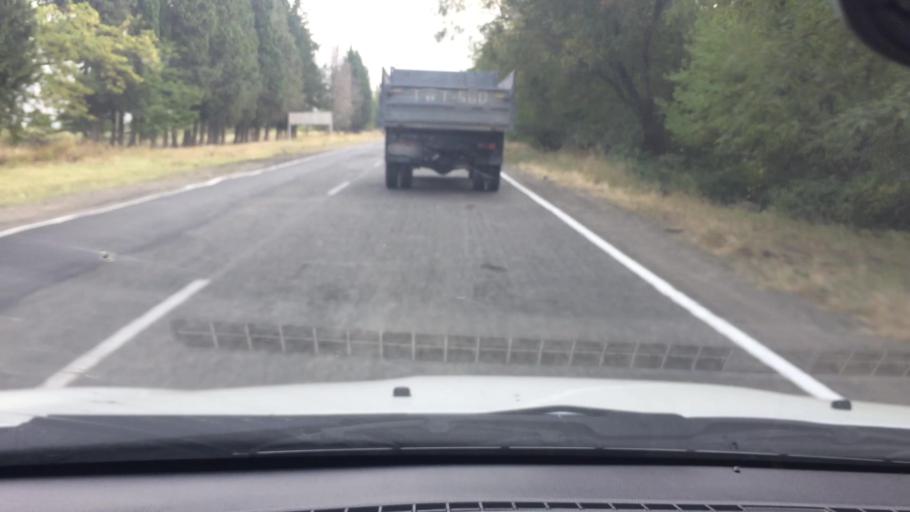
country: GE
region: Kvemo Kartli
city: Rust'avi
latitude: 41.4660
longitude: 44.9826
